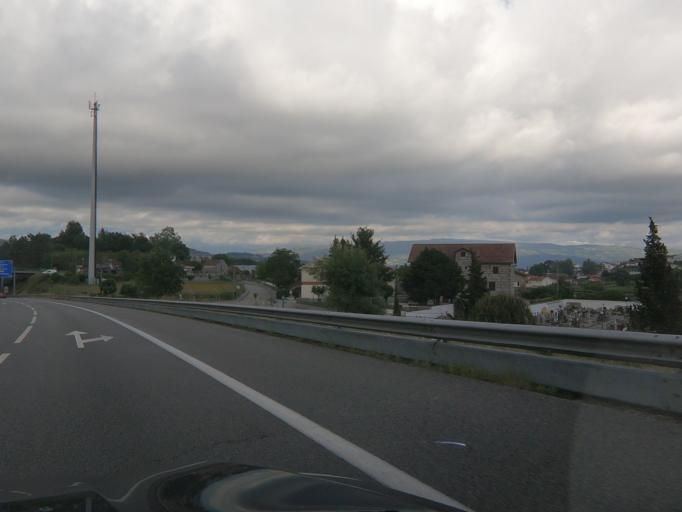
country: PT
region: Porto
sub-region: Lousada
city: Meinedo
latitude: 41.2308
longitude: -8.2114
